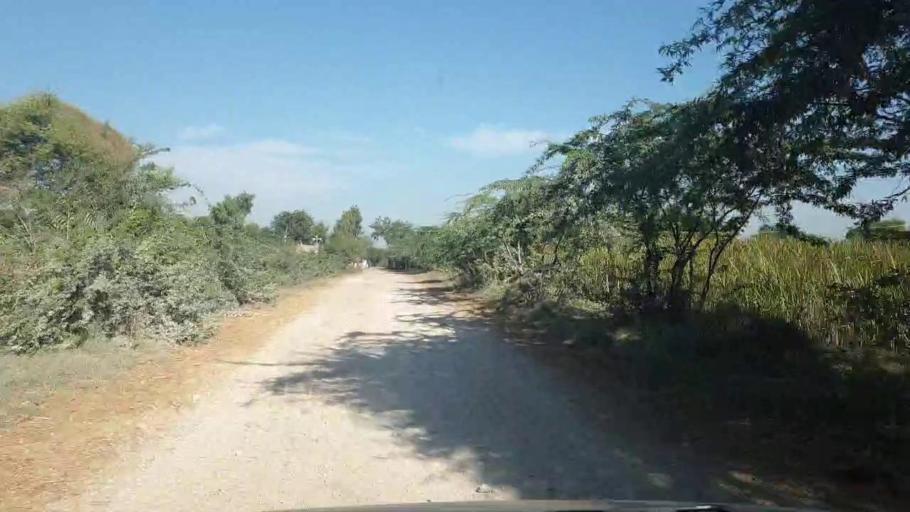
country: PK
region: Sindh
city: Talhar
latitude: 24.9087
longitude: 68.8089
